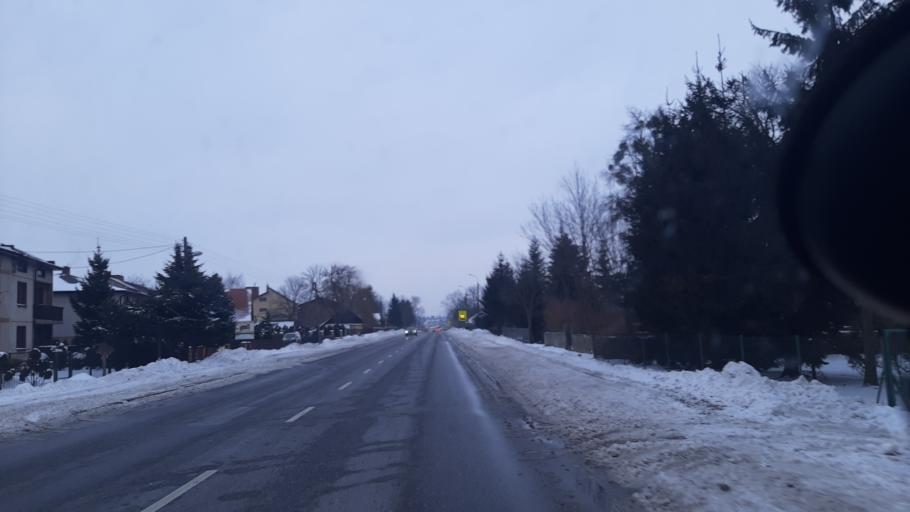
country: PL
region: Lublin Voivodeship
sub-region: Powiat pulawski
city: Markuszow
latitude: 51.3760
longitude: 22.2519
